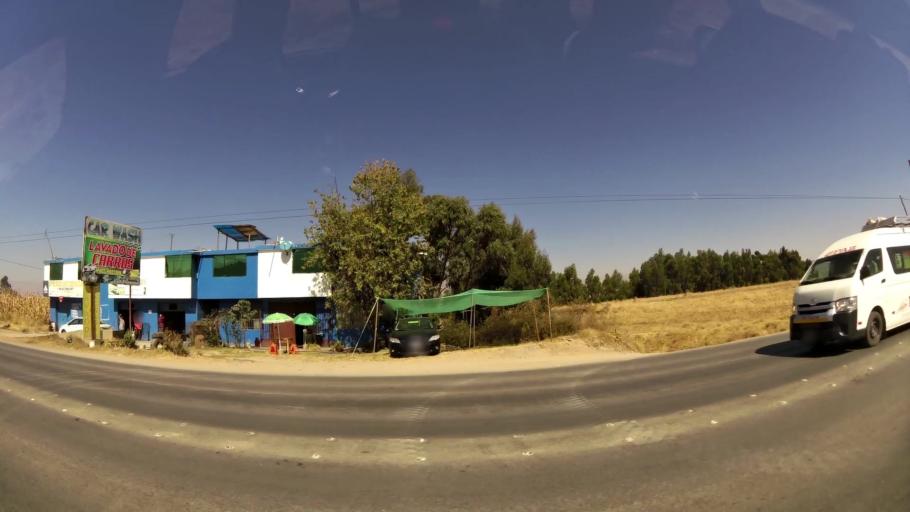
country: PE
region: Junin
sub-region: Provincia de Huancayo
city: San Agustin
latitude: -11.9794
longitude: -75.2639
